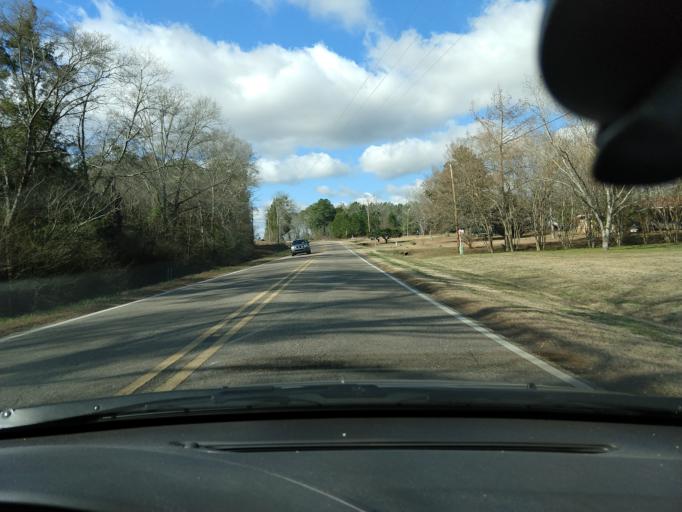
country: US
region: Alabama
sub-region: Coffee County
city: Enterprise
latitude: 31.3241
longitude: -85.8955
